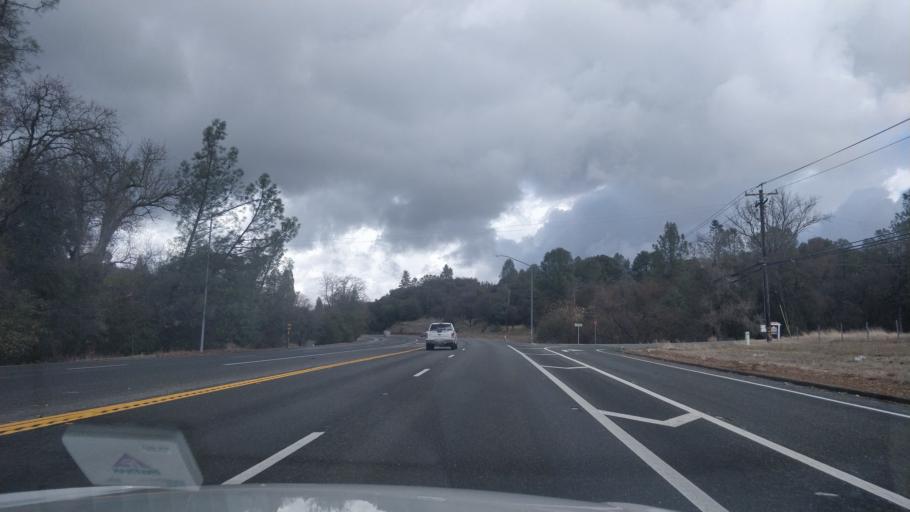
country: US
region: California
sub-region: Nevada County
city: Lake of the Pines
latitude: 39.0173
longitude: -121.1010
